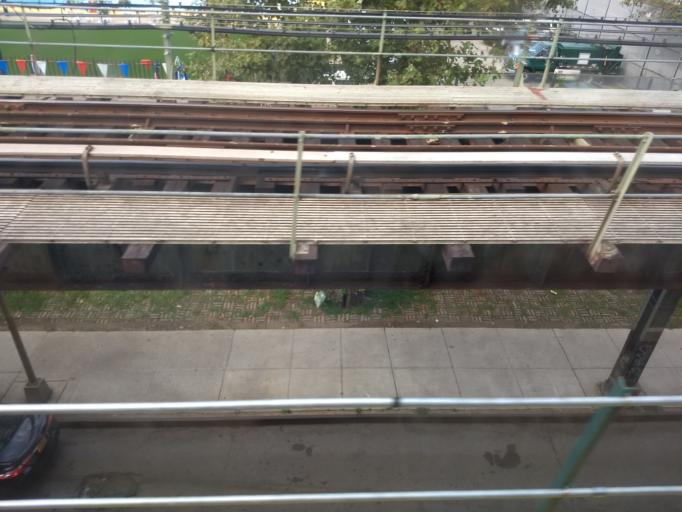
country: US
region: New York
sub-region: Kings County
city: East New York
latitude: 40.6622
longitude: -73.9121
